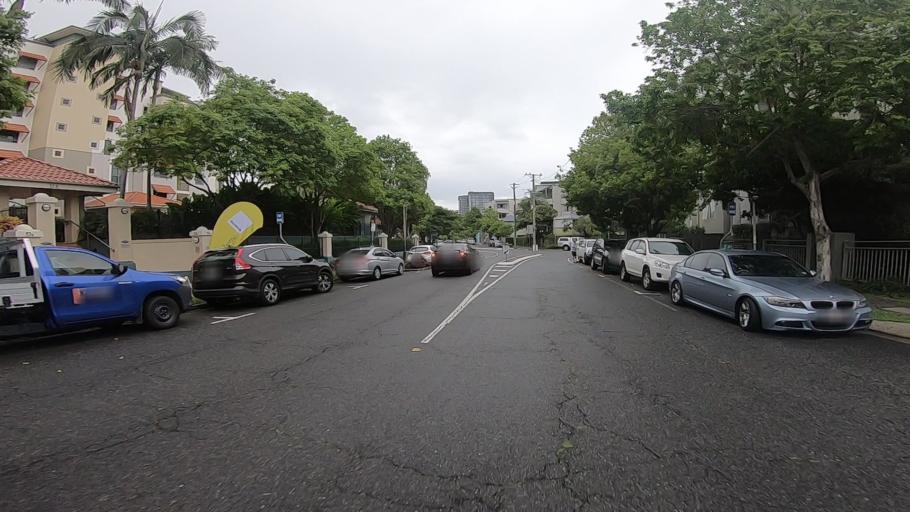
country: AU
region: Queensland
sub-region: Brisbane
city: Ascot
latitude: -27.4448
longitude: 153.0455
